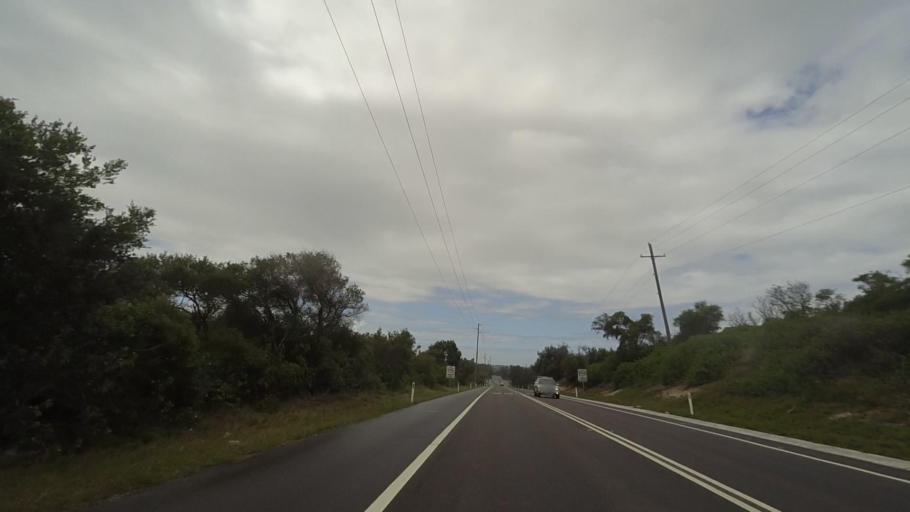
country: AU
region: New South Wales
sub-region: Wyong Shire
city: The Entrance
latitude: -33.3227
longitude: 151.5139
